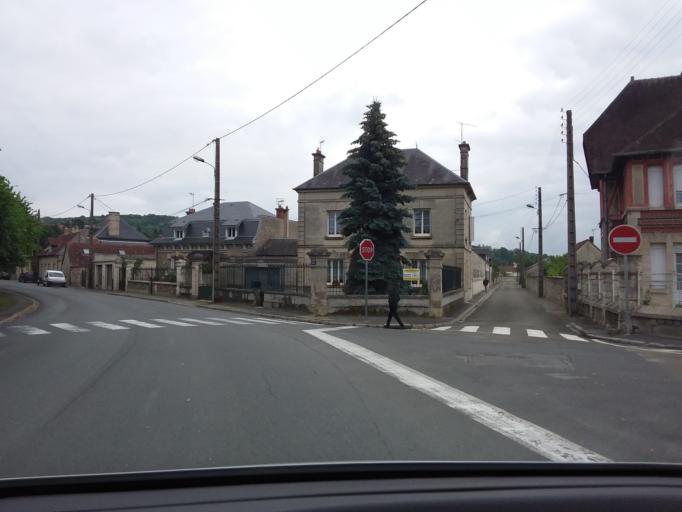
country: FR
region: Picardie
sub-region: Departement de l'Aisne
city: Vailly-sur-Aisne
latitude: 49.4082
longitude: 3.5175
